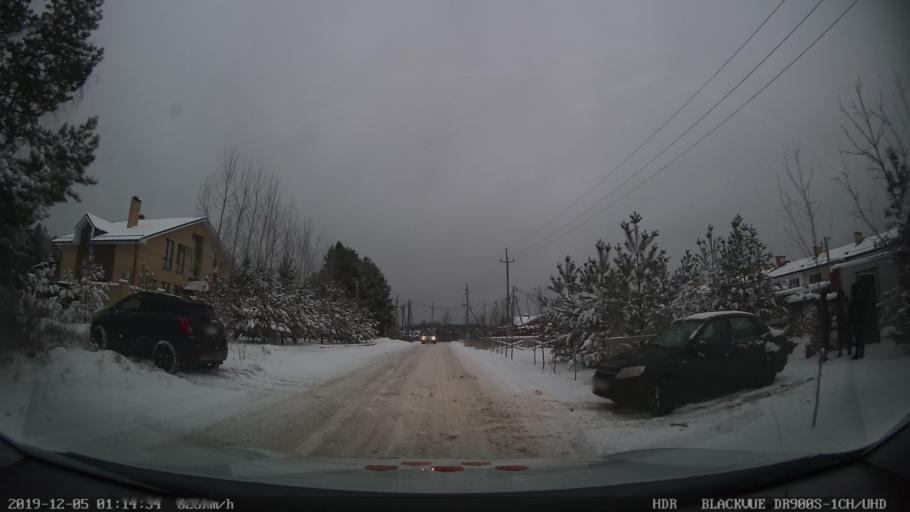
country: RU
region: Tatarstan
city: Stolbishchi
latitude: 55.6428
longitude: 49.1147
